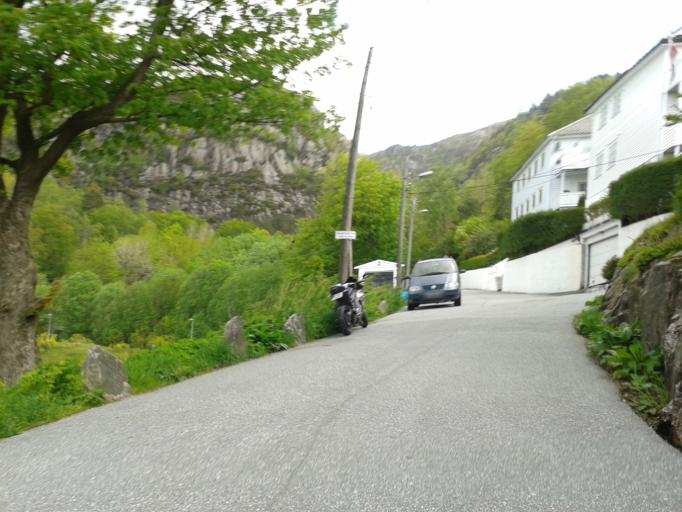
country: NO
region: Hordaland
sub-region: Bergen
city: Bergen
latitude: 60.4179
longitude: 5.3159
